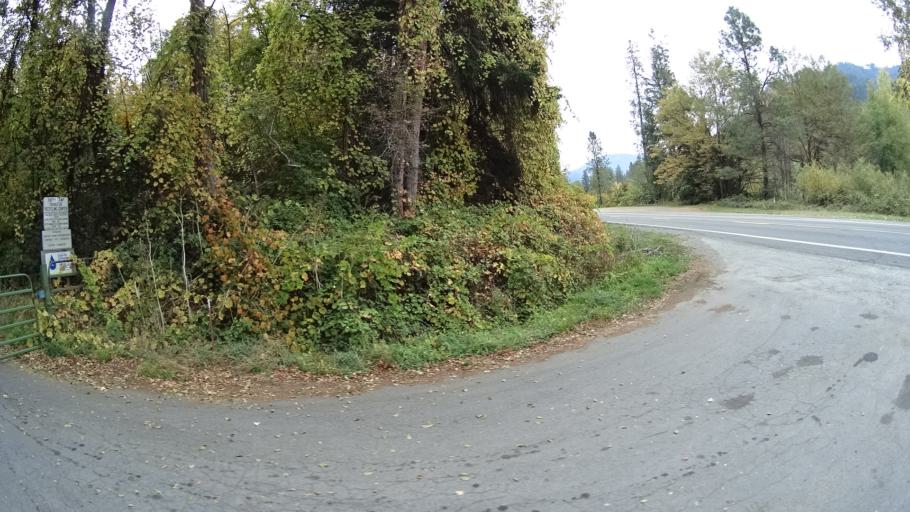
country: US
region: California
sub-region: Siskiyou County
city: Happy Camp
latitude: 41.7797
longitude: -123.3964
